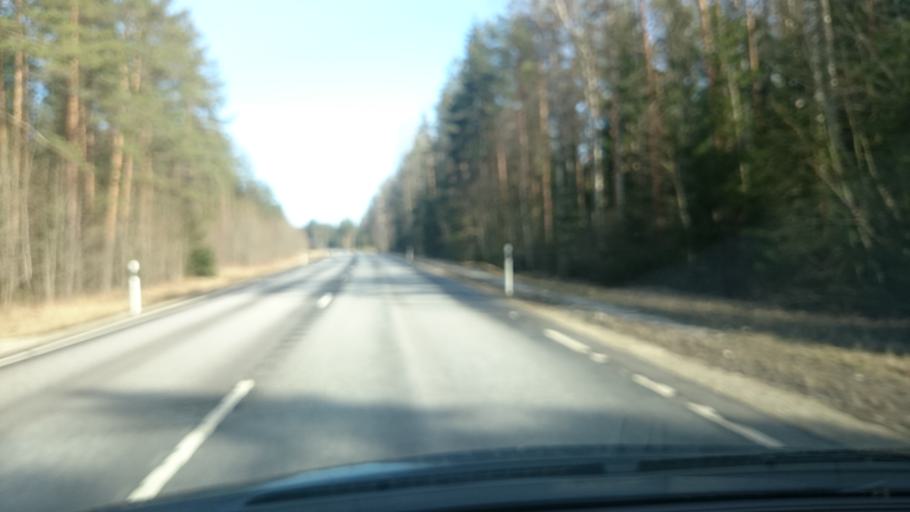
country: EE
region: Paernumaa
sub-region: Vaendra vald (alev)
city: Vandra
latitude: 58.6763
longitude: 25.2215
